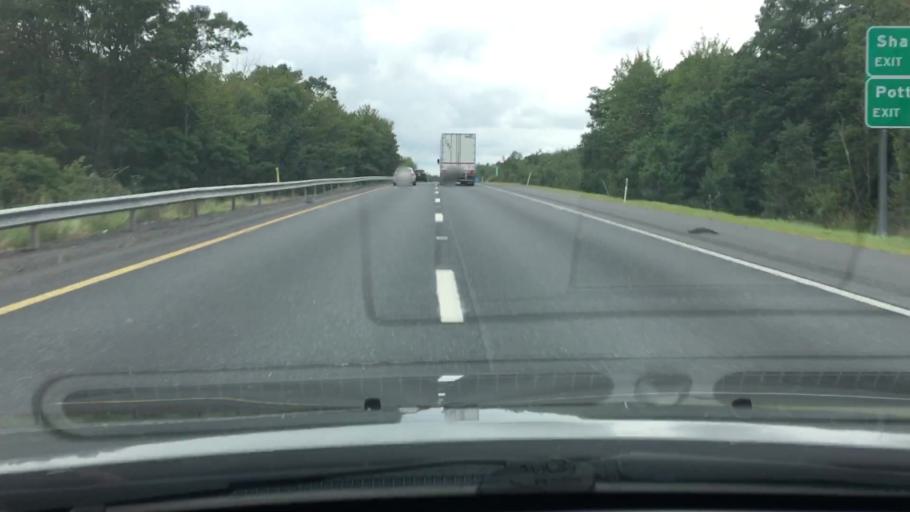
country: US
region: Pennsylvania
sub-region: Schuylkill County
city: Frackville
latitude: 40.7773
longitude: -76.1914
